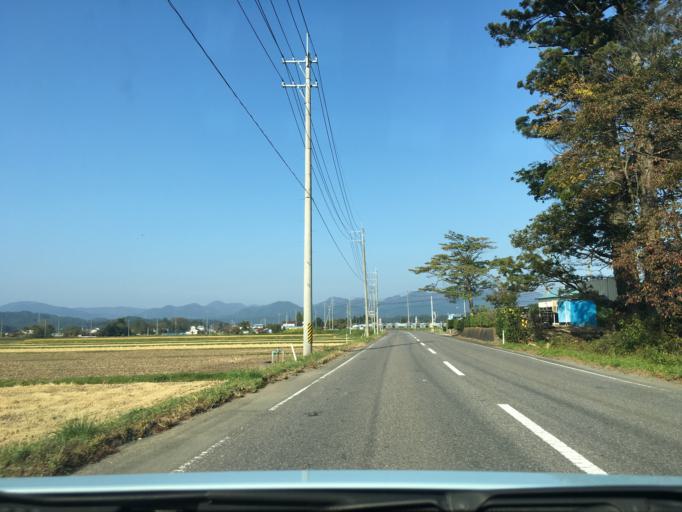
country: JP
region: Fukushima
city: Sukagawa
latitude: 37.2799
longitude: 140.2673
